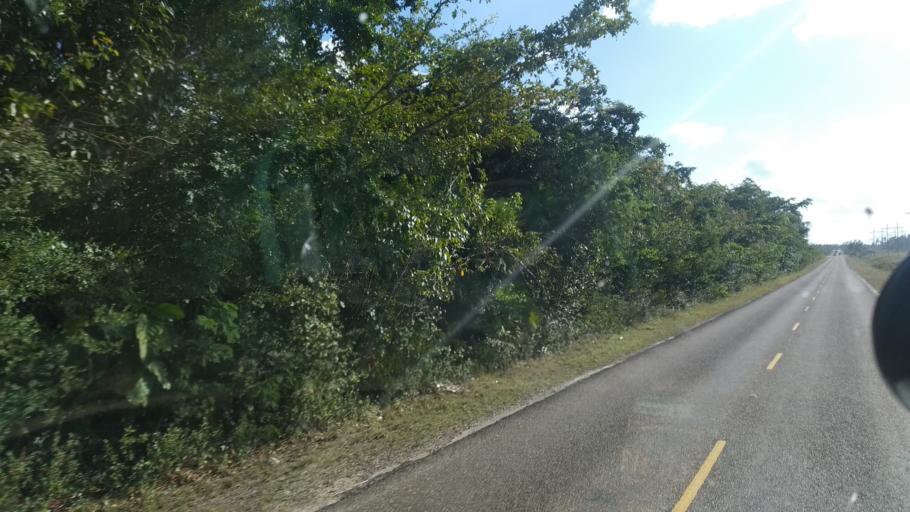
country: BZ
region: Cayo
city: Belmopan
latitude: 17.3641
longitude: -88.5410
